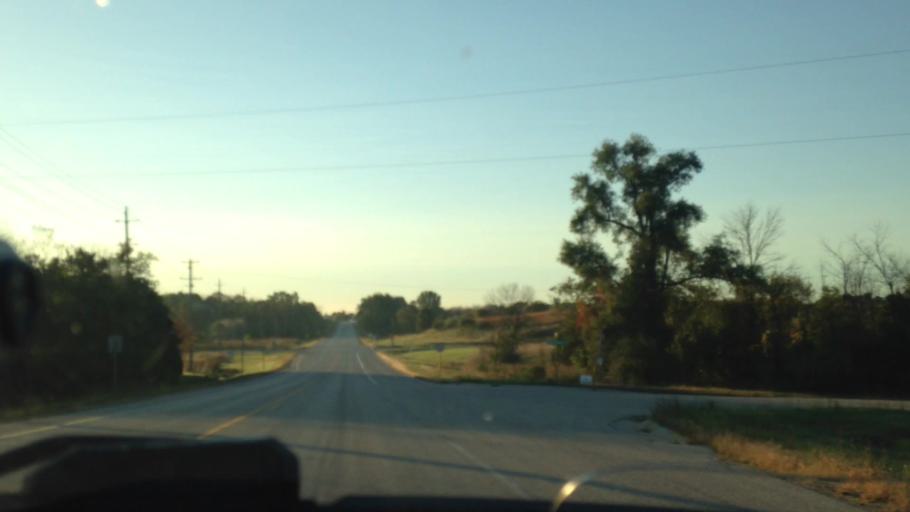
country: US
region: Wisconsin
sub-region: Ozaukee County
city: Saukville
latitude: 43.3971
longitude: -87.9815
